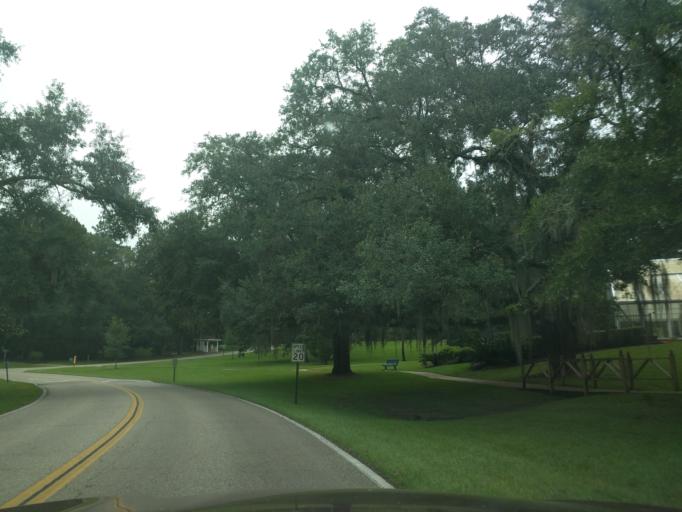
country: US
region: Florida
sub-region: Leon County
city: Tallahassee
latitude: 30.4774
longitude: -84.2061
